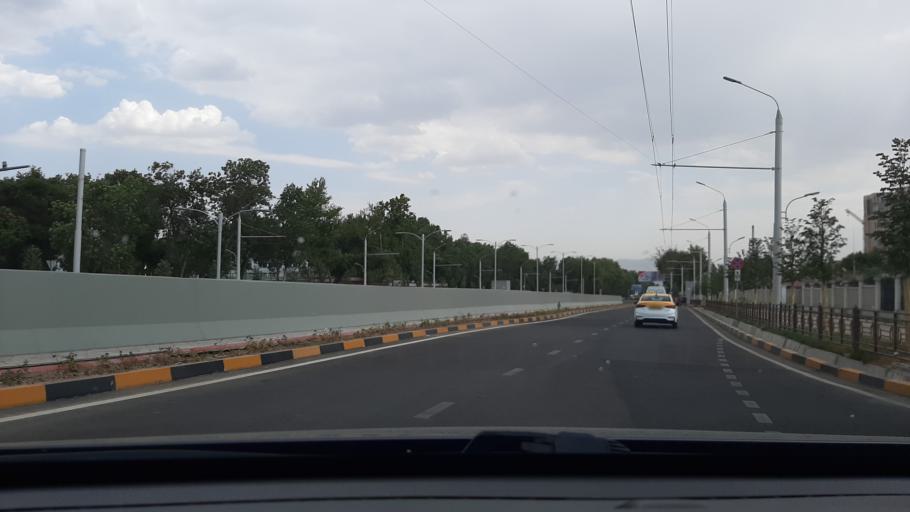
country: TJ
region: Dushanbe
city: Dushanbe
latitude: 38.5838
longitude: 68.7549
